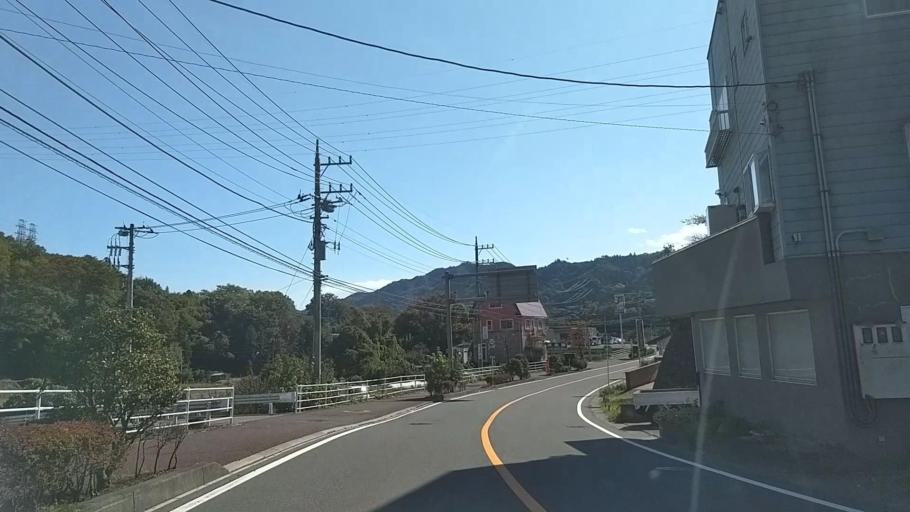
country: JP
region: Yamanashi
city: Uenohara
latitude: 35.6203
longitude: 139.1090
